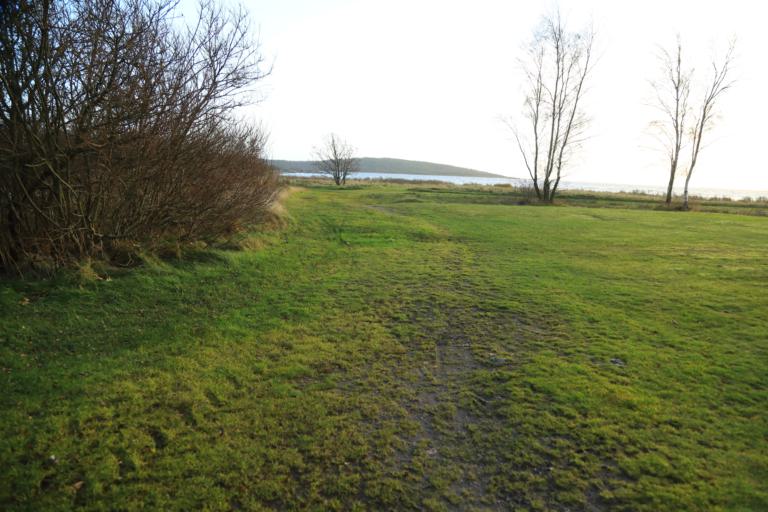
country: SE
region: Halland
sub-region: Varbergs Kommun
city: Varberg
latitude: 57.1916
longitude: 12.2023
